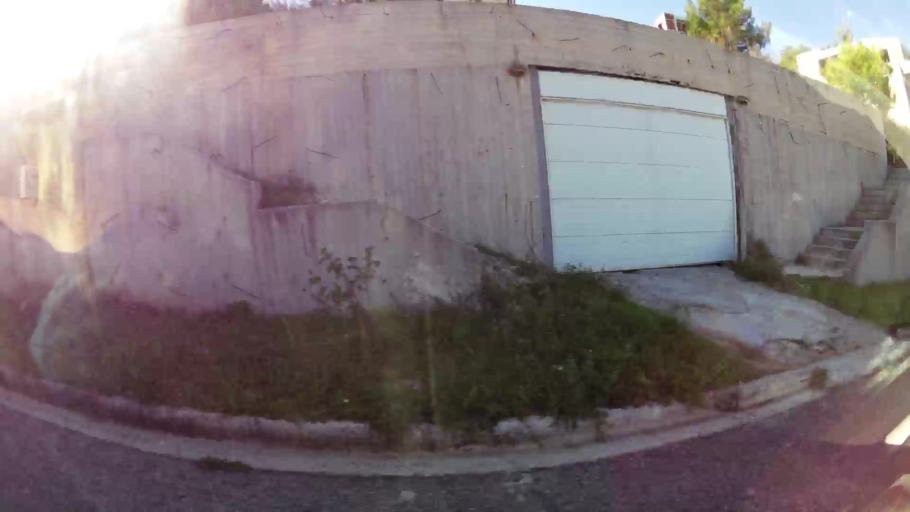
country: GR
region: Attica
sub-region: Nomarchia Anatolikis Attikis
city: Dhrafi
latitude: 38.0324
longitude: 23.8950
